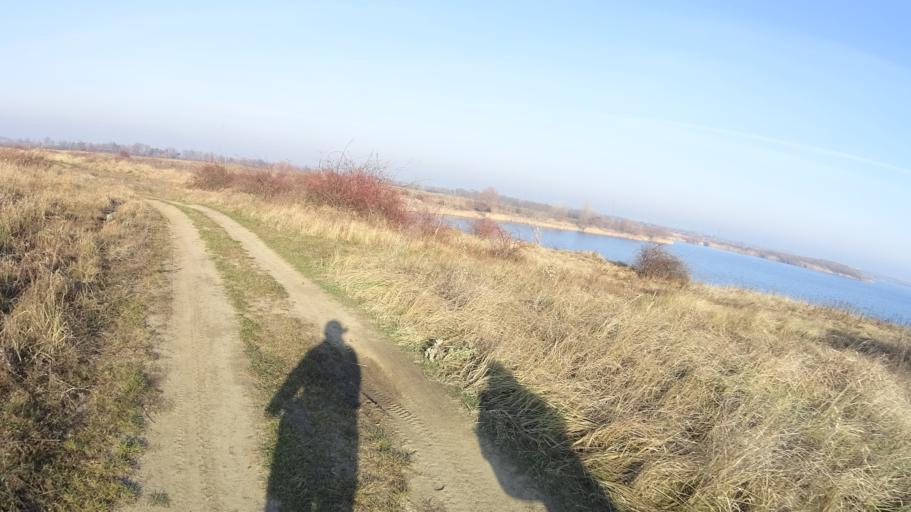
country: HU
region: Borsod-Abauj-Zemplen
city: Nyekladhaza
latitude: 47.9911
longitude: 20.8695
